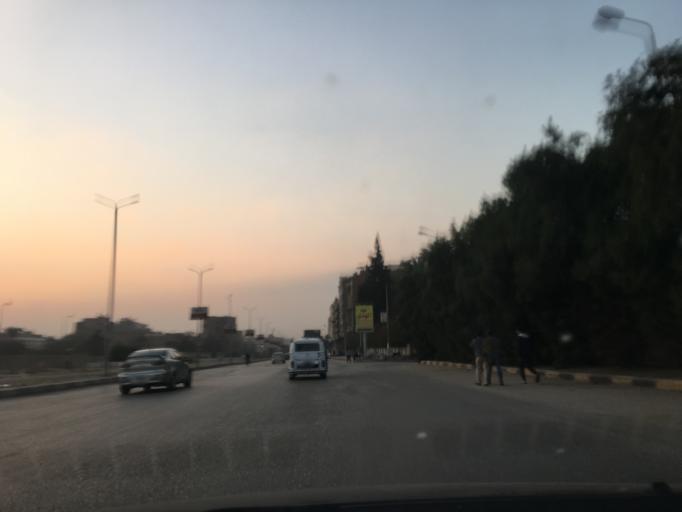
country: EG
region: Al Jizah
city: Al Jizah
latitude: 29.9890
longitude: 31.1389
